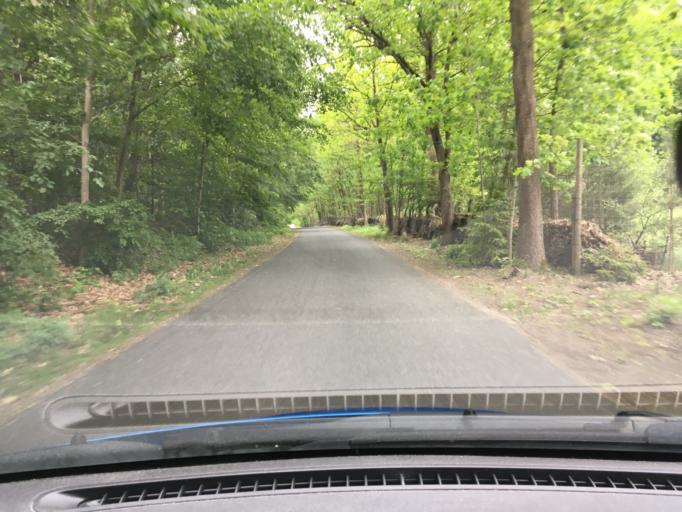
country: DE
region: Lower Saxony
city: Bispingen
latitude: 53.0713
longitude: 10.0107
